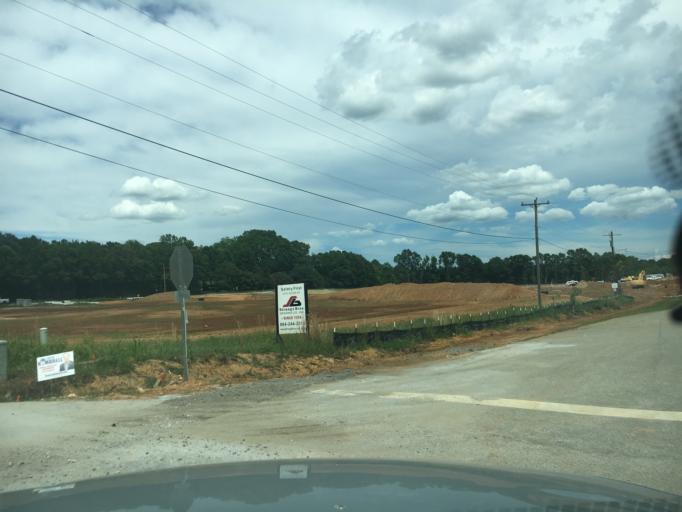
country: US
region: South Carolina
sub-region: Spartanburg County
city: Duncan
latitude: 34.8605
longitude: -82.1100
